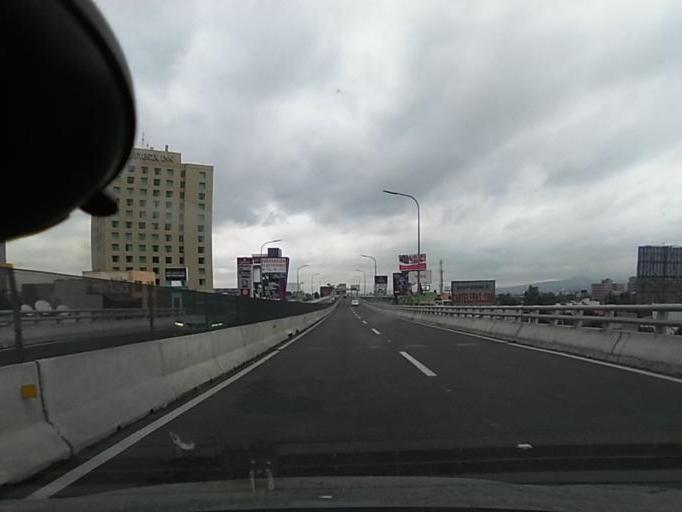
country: MX
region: Mexico City
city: Tlalpan
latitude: 19.3020
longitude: -99.1677
